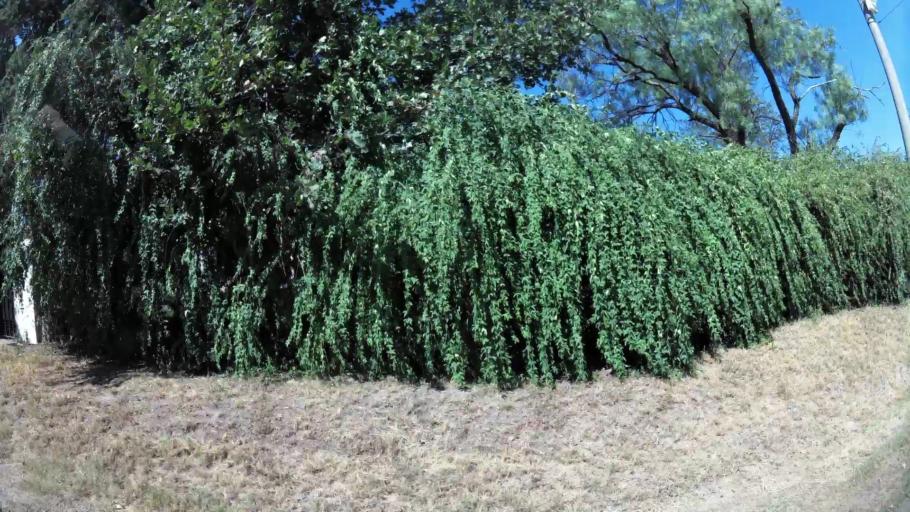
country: AR
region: Cordoba
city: Villa Allende
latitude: -31.2946
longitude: -64.2823
